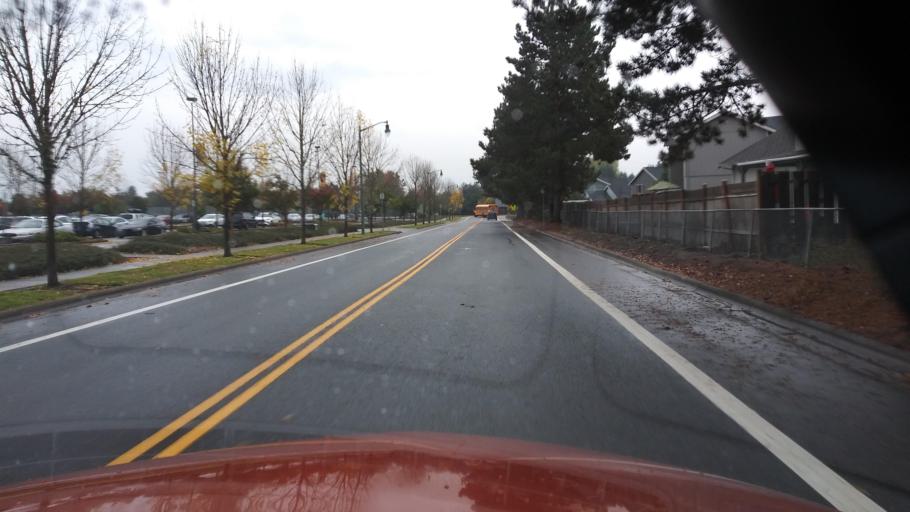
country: US
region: Oregon
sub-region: Washington County
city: Forest Grove
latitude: 45.5338
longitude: -123.1205
